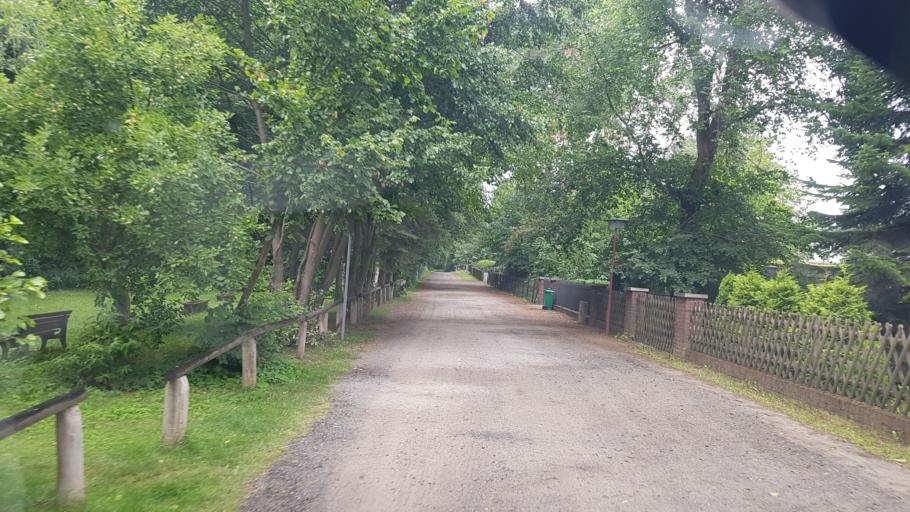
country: DE
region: Brandenburg
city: Gross Koris
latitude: 52.1716
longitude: 13.6989
